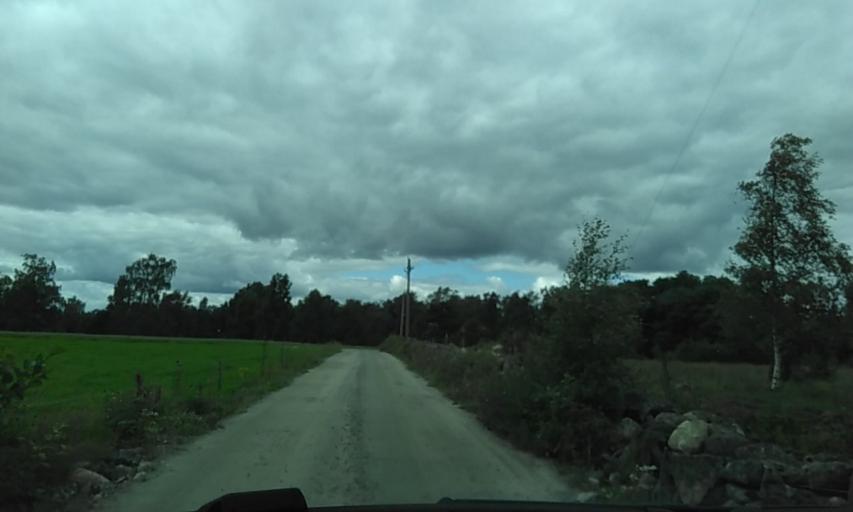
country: SE
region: Vaestra Goetaland
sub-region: Boras Kommun
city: Sjomarken
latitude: 57.7953
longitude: 12.8676
